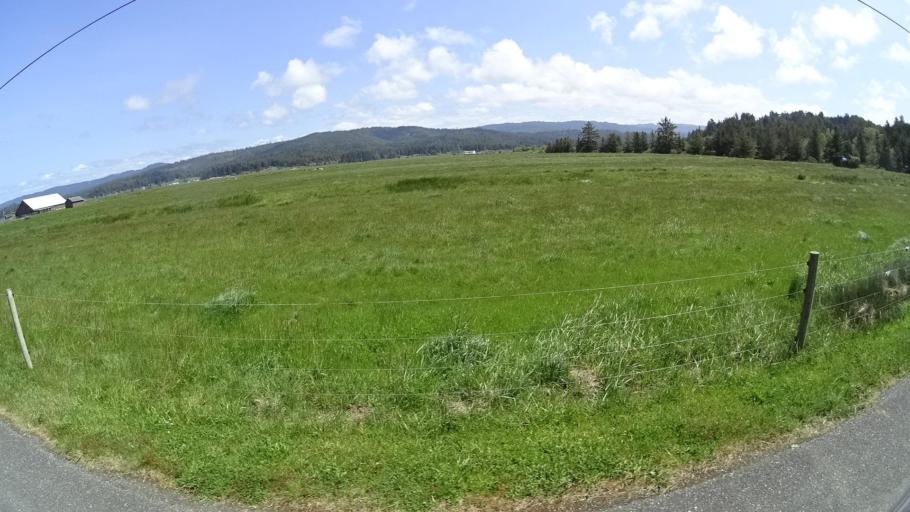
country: US
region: California
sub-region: Humboldt County
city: Myrtletown
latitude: 40.7891
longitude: -124.1091
